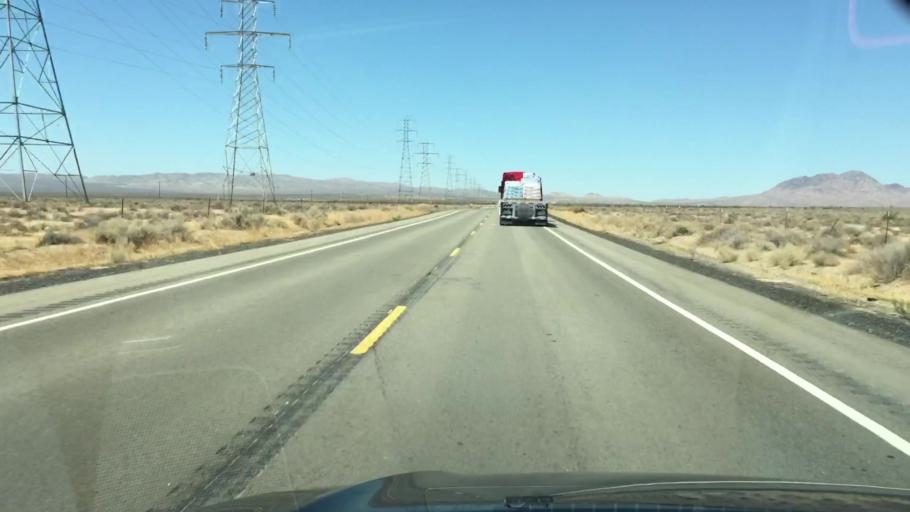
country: US
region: California
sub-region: Kern County
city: Boron
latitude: 35.2147
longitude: -117.6036
